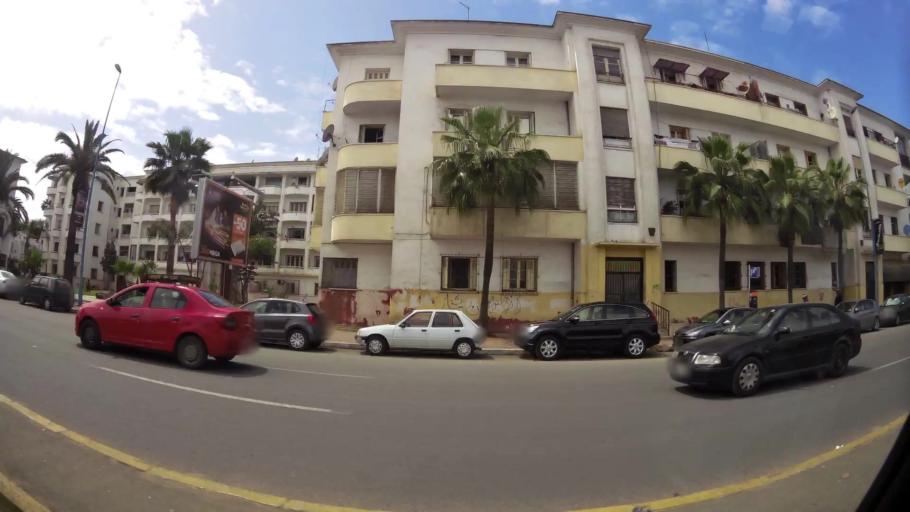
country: MA
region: Grand Casablanca
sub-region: Casablanca
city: Casablanca
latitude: 33.5953
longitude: -7.6380
